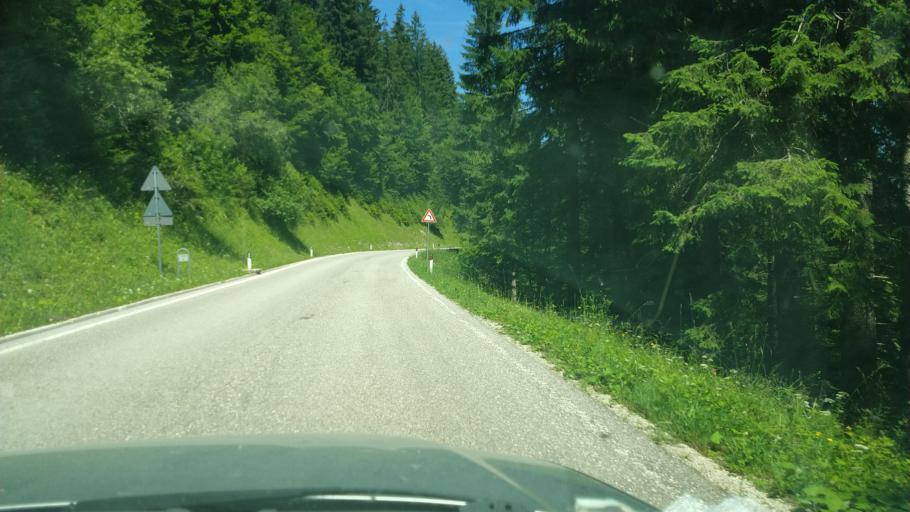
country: IT
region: Trentino-Alto Adige
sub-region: Provincia di Trento
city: Folgaria
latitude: 45.9057
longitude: 11.2195
